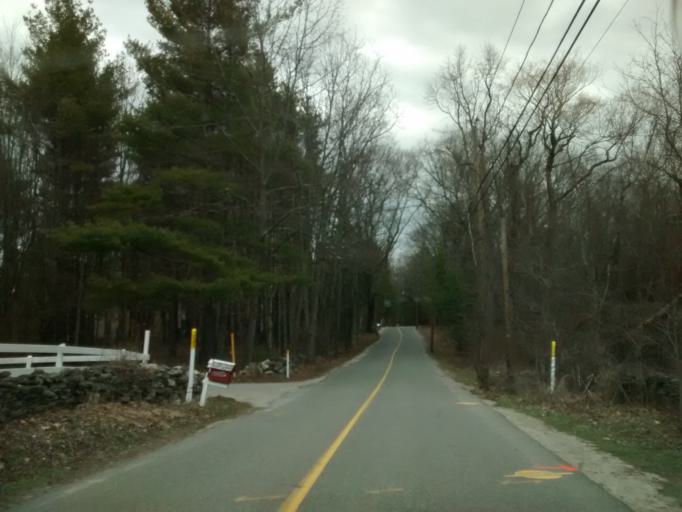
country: US
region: Massachusetts
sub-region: Worcester County
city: Southbridge
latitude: 42.1162
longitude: -72.0211
